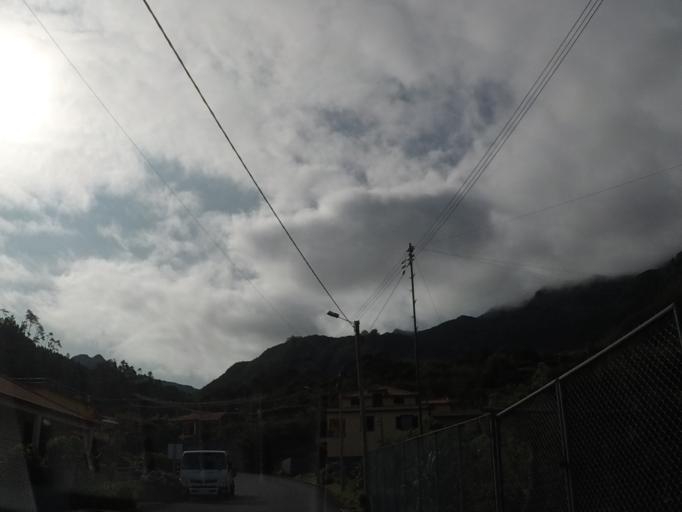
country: PT
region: Madeira
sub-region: Sao Vicente
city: Sao Vicente
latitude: 32.7816
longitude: -17.0437
